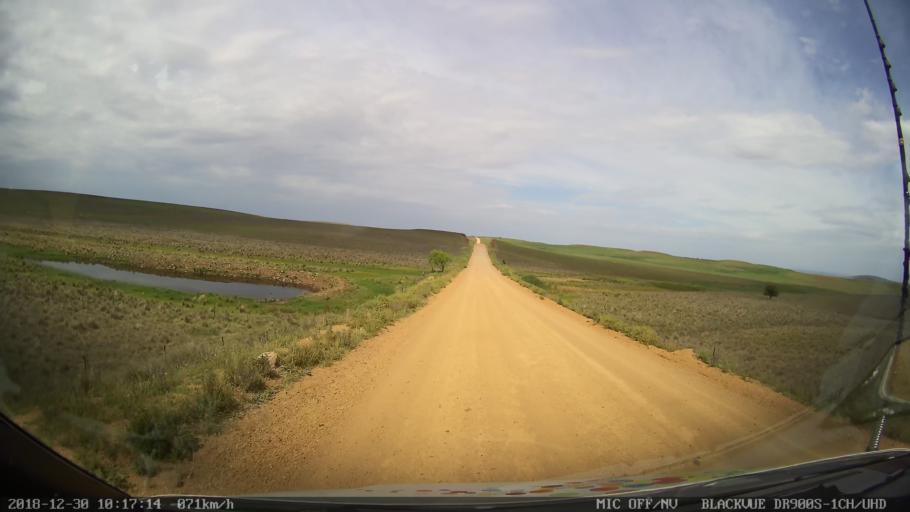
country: AU
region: New South Wales
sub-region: Snowy River
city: Berridale
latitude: -36.5480
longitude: 149.0237
